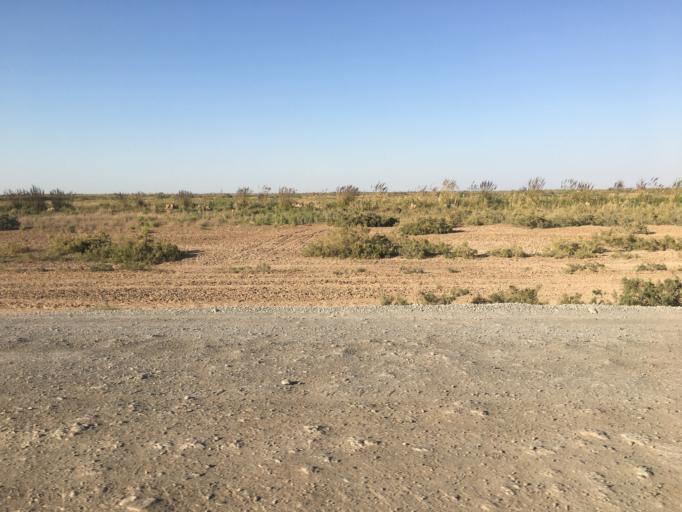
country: IR
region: Razavi Khorasan
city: Sarakhs
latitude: 37.0427
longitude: 61.3141
